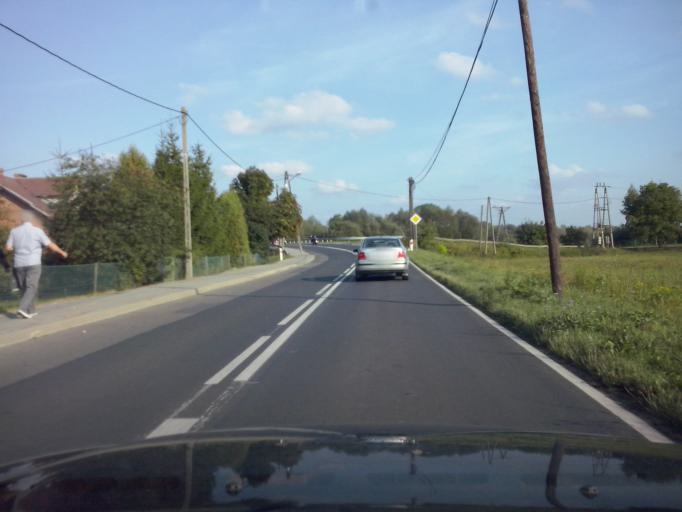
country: PL
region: Subcarpathian Voivodeship
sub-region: Powiat nizanski
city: Krzeszow
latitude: 50.4013
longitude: 22.3291
